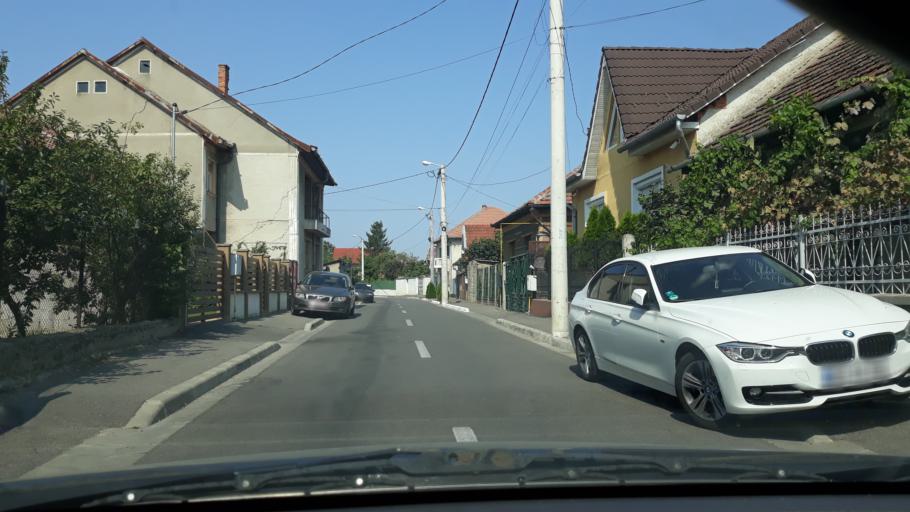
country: RO
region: Bihor
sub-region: Comuna Biharea
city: Oradea
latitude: 47.0411
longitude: 21.9518
